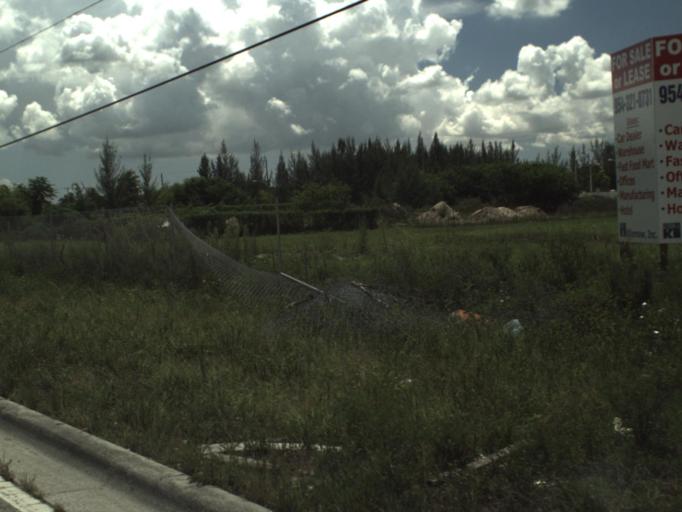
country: US
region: Florida
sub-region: Broward County
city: Tamarac
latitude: 26.1936
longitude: -80.2917
